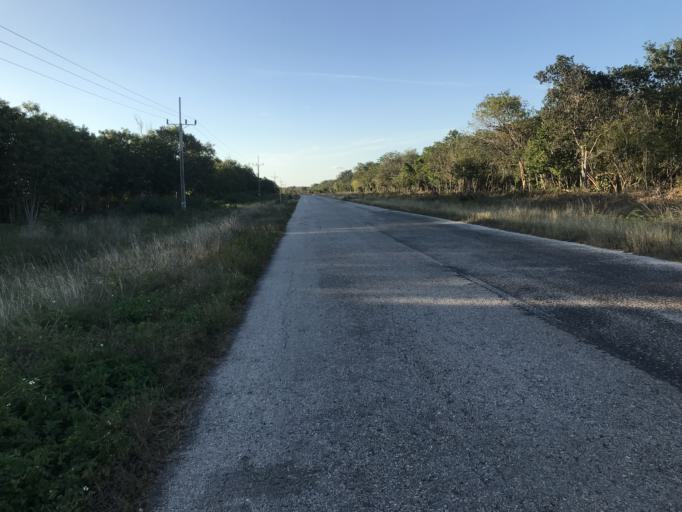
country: CU
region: Cienfuegos
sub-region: Municipio de Aguada de Pasajeros
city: Aguada de Pasajeros
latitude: 22.0737
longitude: -81.0579
